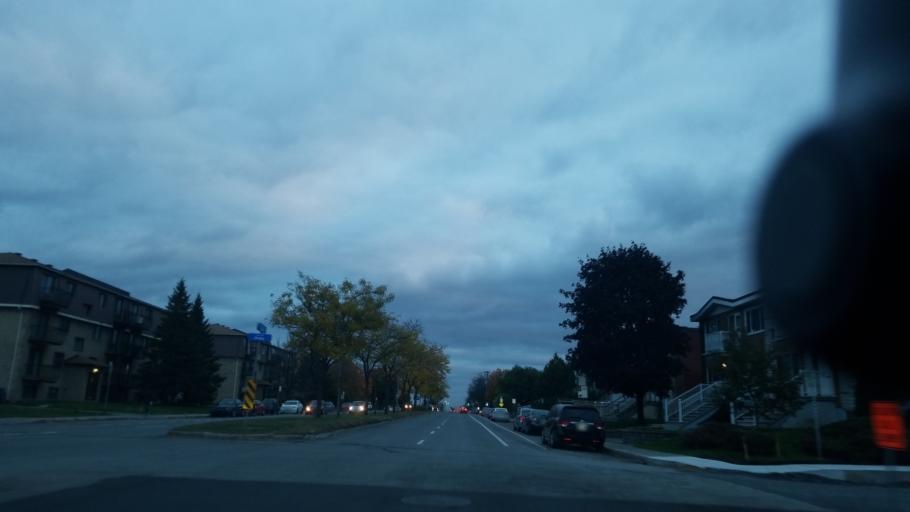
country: CA
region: Quebec
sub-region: Laval
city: Laval
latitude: 45.5626
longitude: -73.7159
